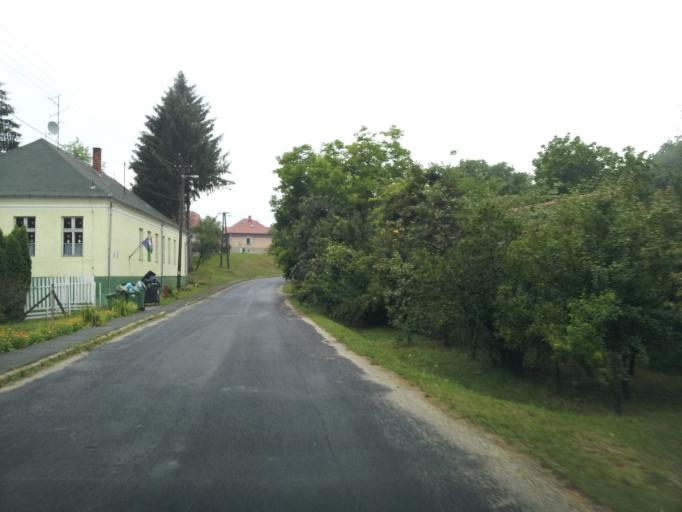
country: HU
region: Zala
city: Zalalovo
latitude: 46.8672
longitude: 16.5476
